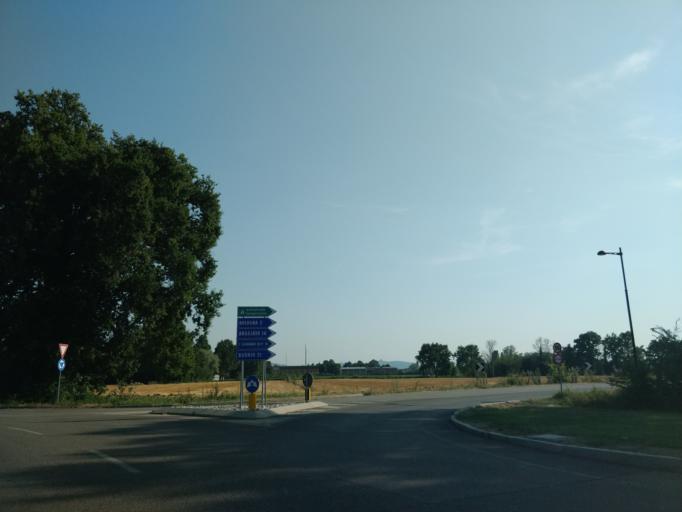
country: IT
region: Emilia-Romagna
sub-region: Provincia di Bologna
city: Progresso
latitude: 44.5609
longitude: 11.3505
